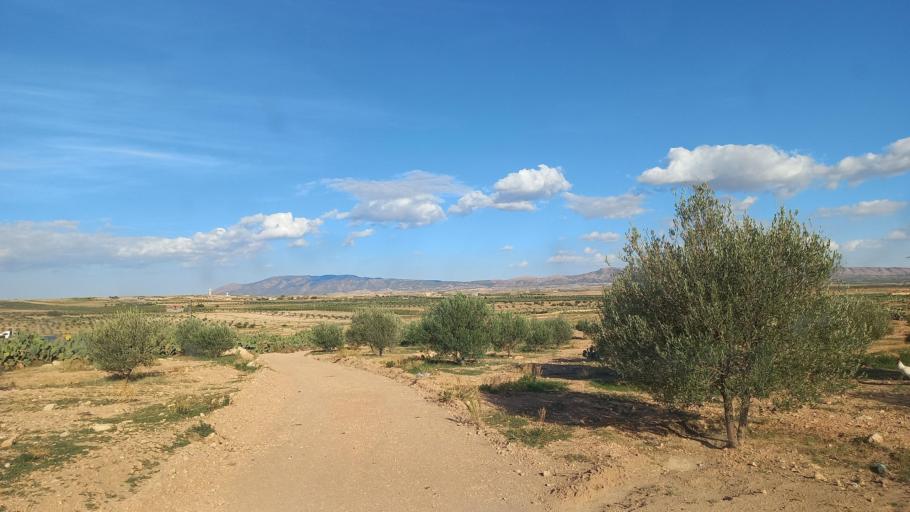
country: TN
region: Al Qasrayn
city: Sbiba
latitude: 35.3840
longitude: 9.0247
